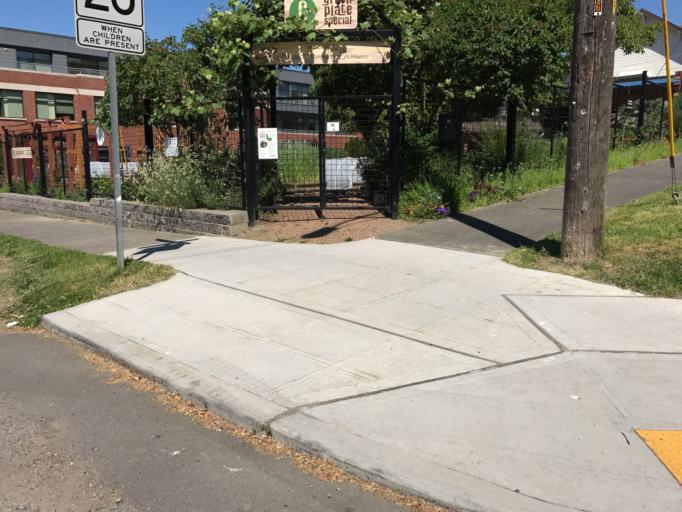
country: US
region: Washington
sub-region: King County
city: Seattle
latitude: 47.5837
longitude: -122.3003
